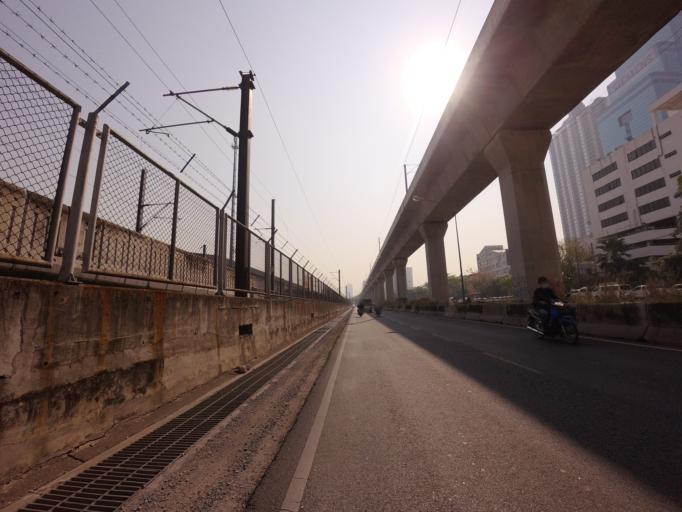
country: TH
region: Bangkok
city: Watthana
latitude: 13.7451
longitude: 100.5878
